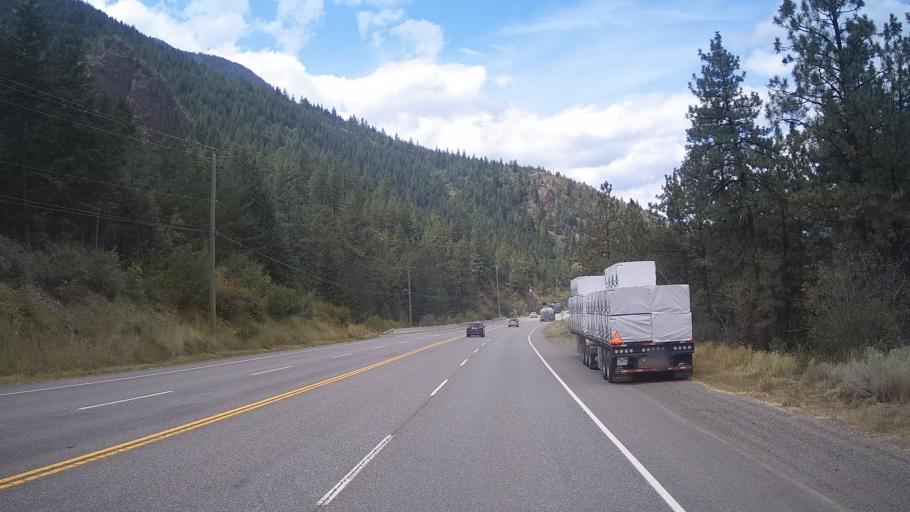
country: CA
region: British Columbia
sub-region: Thompson-Nicola Regional District
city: Ashcroft
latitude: 50.2462
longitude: -121.4892
